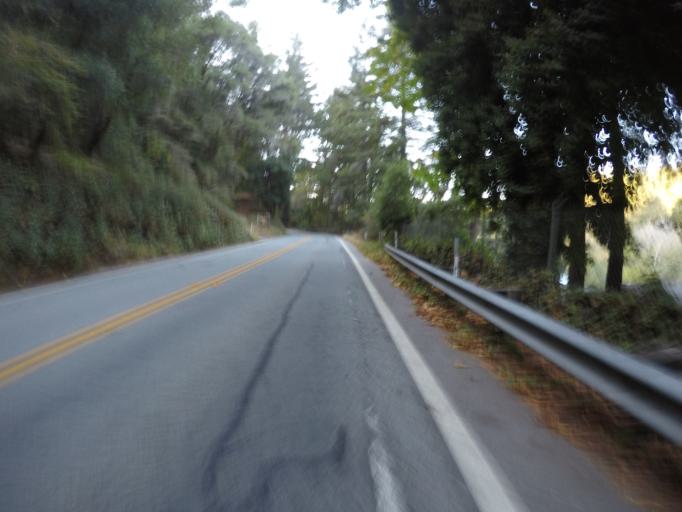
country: US
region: California
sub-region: Santa Cruz County
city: Pasatiempo
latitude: 37.0031
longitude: -122.0391
